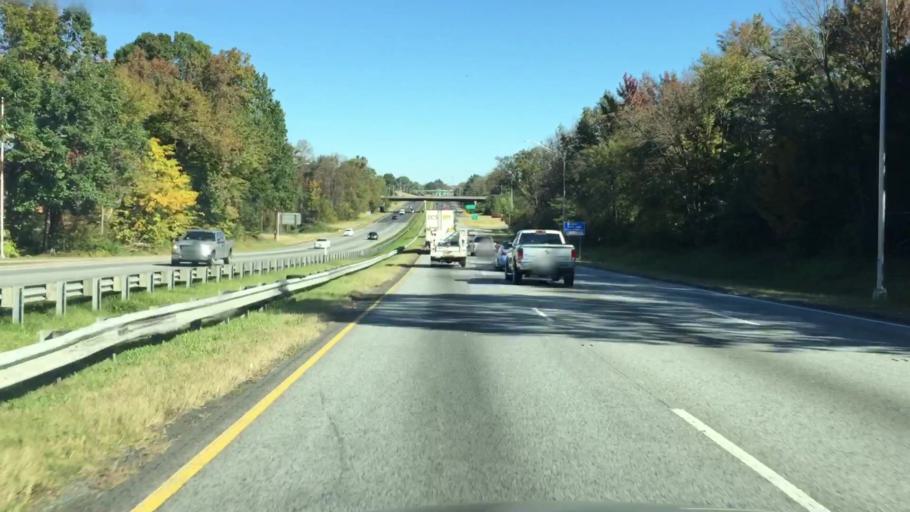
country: US
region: North Carolina
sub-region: Guilford County
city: Greensboro
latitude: 36.1029
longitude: -79.7630
